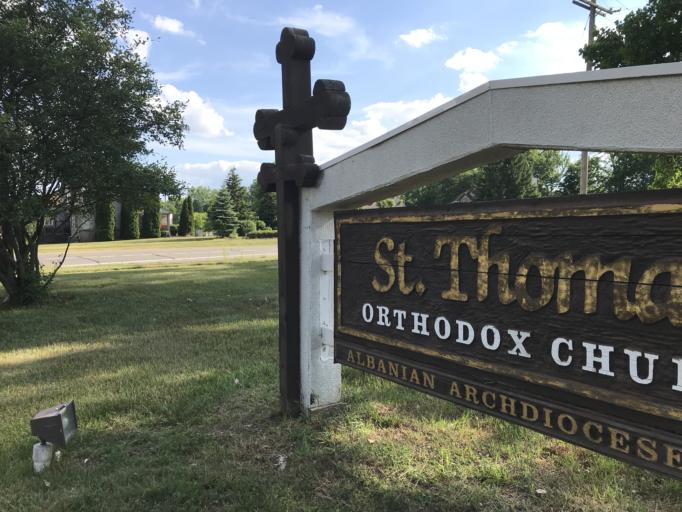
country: US
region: Michigan
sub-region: Oakland County
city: Farmington
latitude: 42.4710
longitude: -83.3336
